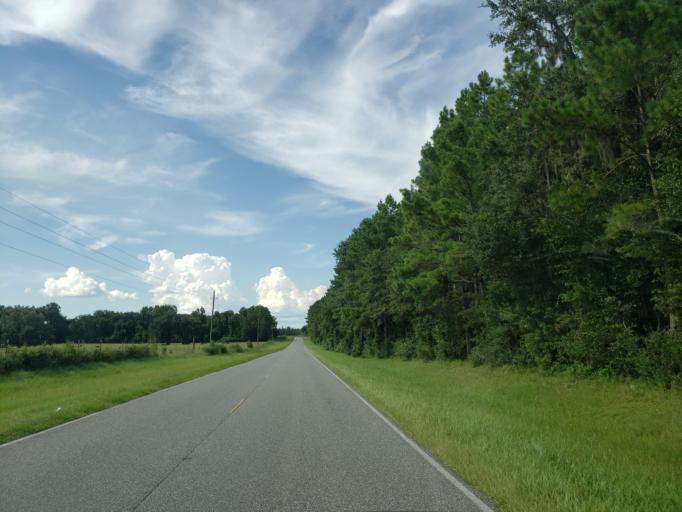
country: US
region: Florida
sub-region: Madison County
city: Madison
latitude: 30.5926
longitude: -83.2242
